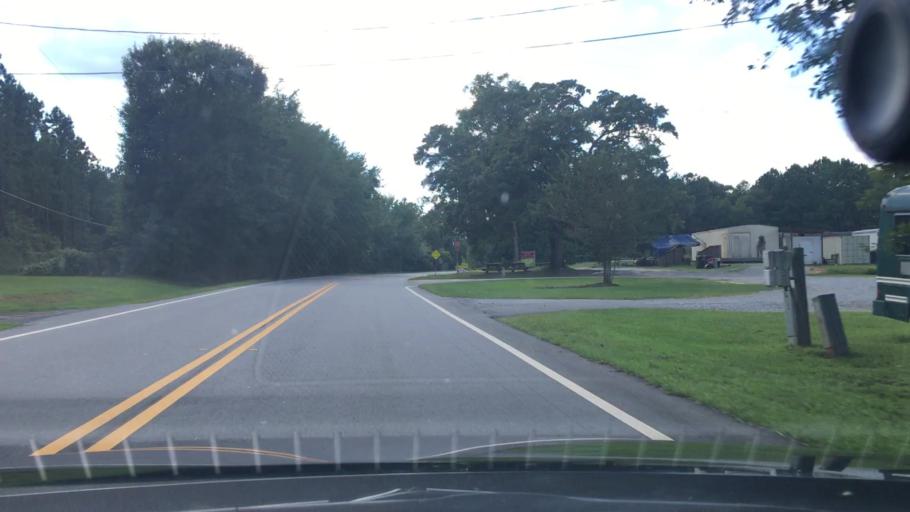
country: US
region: Georgia
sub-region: Butts County
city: Indian Springs
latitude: 33.2864
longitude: -83.8865
